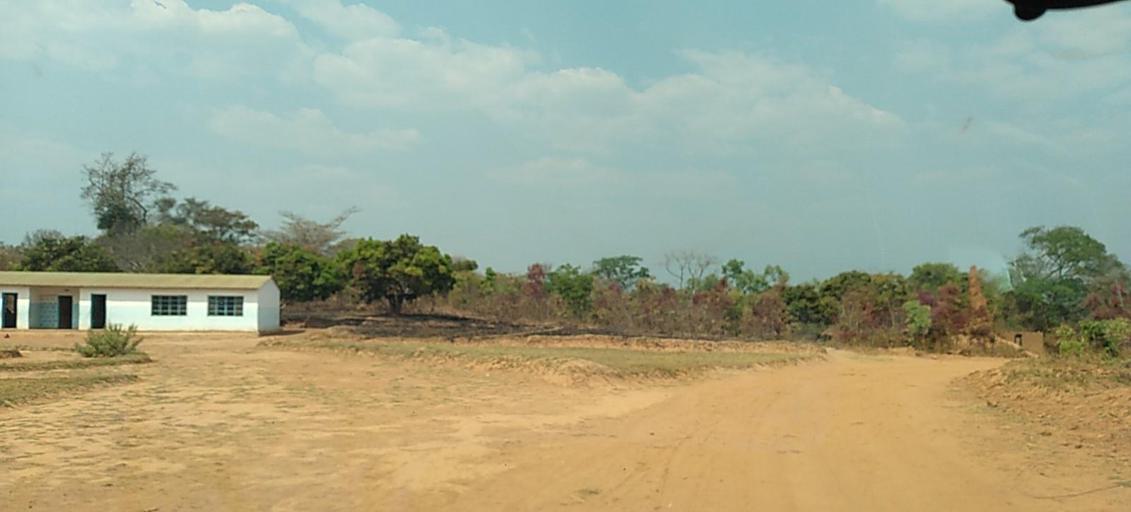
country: ZM
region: North-Western
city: Kasempa
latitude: -13.3045
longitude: 26.0776
